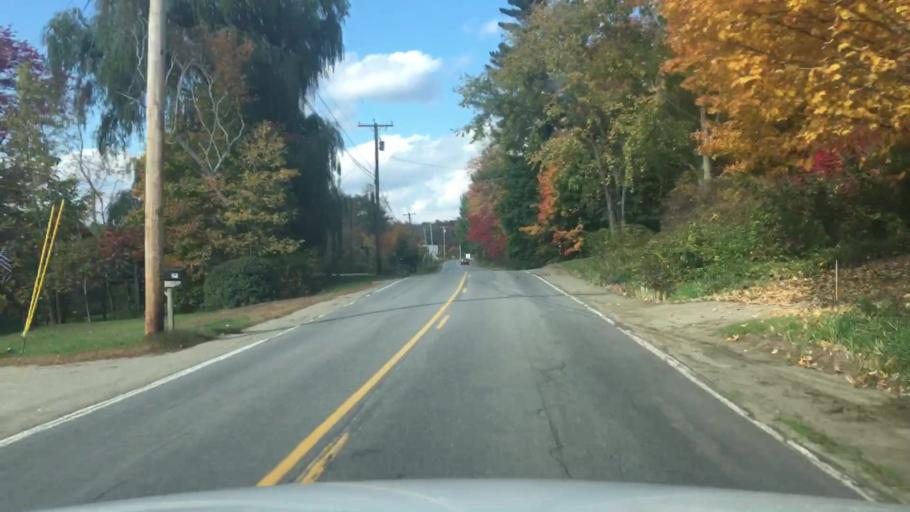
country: US
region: Maine
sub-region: Knox County
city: Union
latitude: 44.2083
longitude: -69.2624
